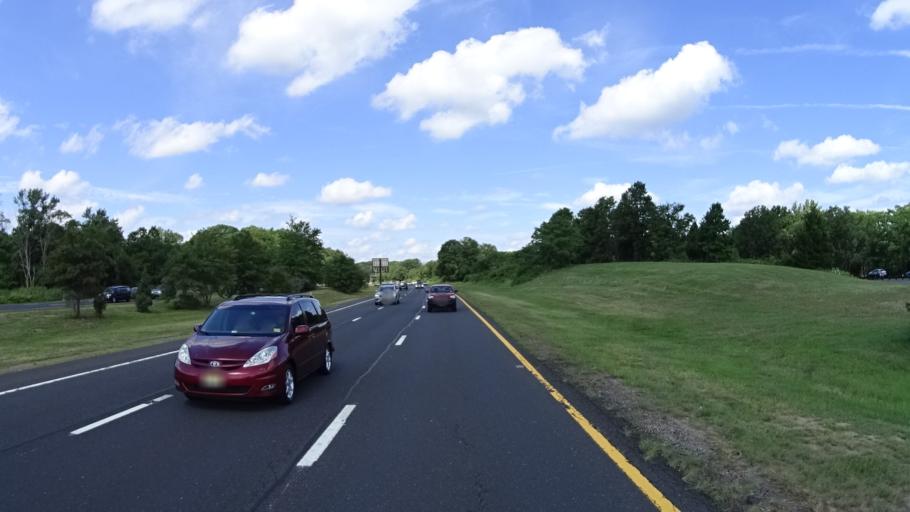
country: US
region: New Jersey
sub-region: Monmouth County
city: Matawan
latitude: 40.4267
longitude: -74.2242
